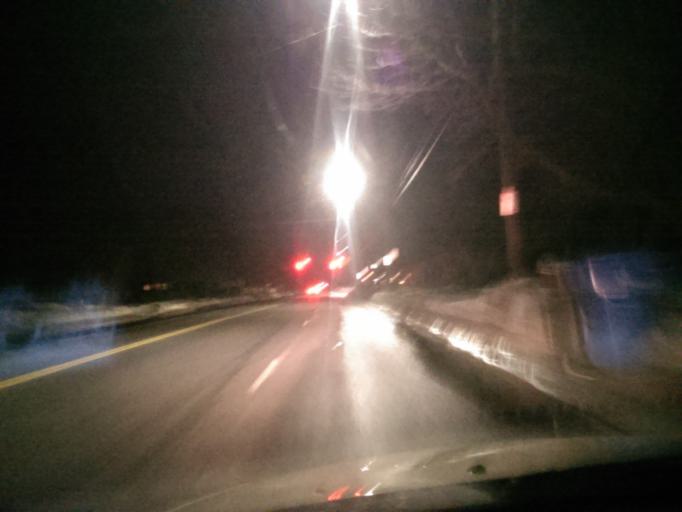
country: US
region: Massachusetts
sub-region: Hampden County
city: Ludlow
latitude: 42.1331
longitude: -72.4957
